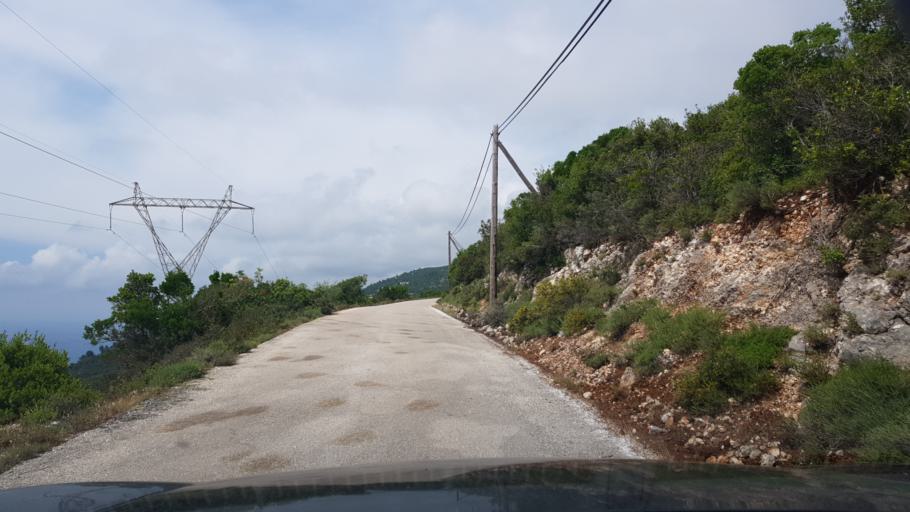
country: GR
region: Ionian Islands
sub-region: Lefkada
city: Nidri
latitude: 38.6057
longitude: 20.5607
